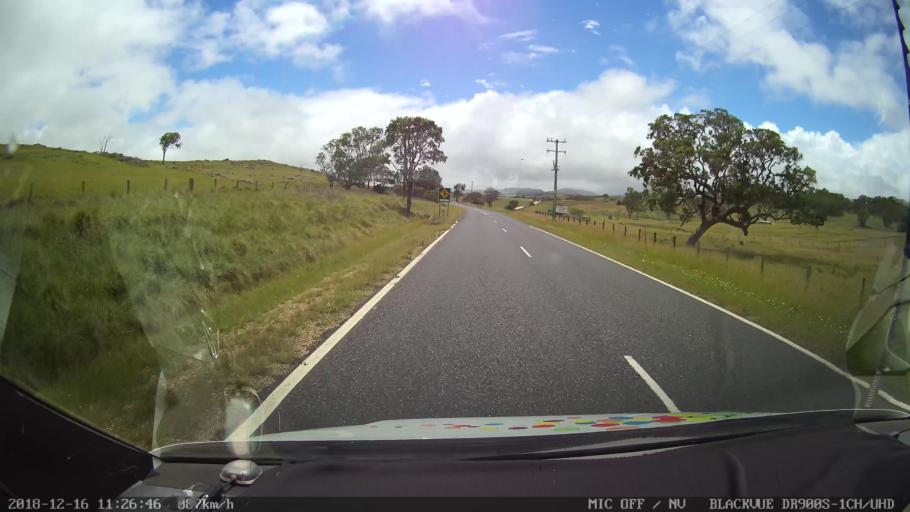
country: AU
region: New South Wales
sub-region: Tenterfield Municipality
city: Carrolls Creek
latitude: -29.0499
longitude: 152.0786
